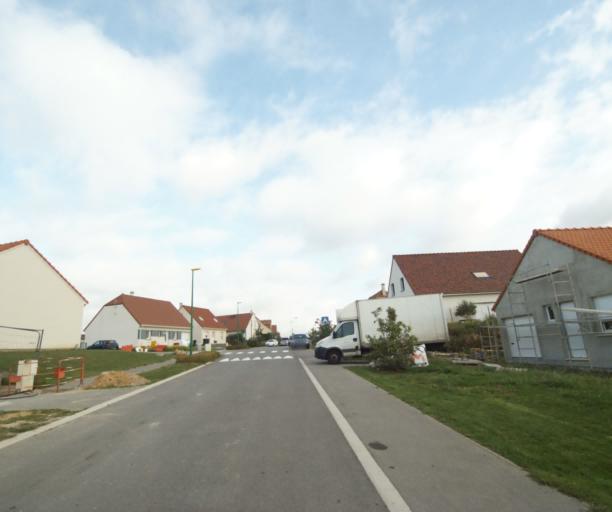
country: FR
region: Nord-Pas-de-Calais
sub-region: Departement du Pas-de-Calais
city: Etaples
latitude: 50.5137
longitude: 1.6568
